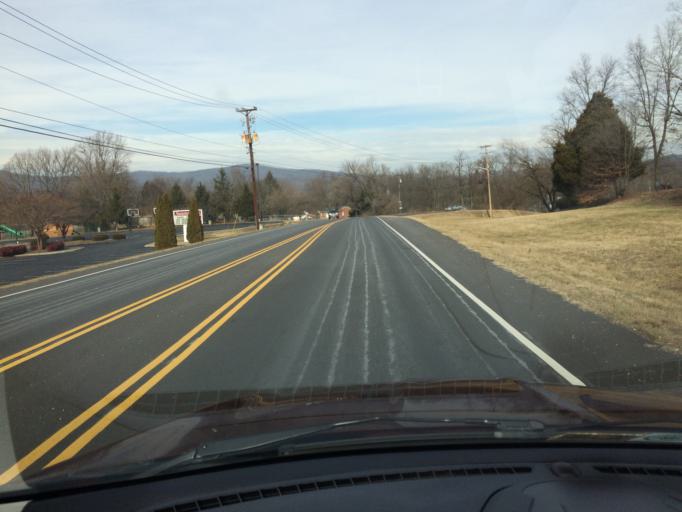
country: US
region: Virginia
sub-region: Roanoke County
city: Hollins
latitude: 37.3398
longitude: -79.9425
